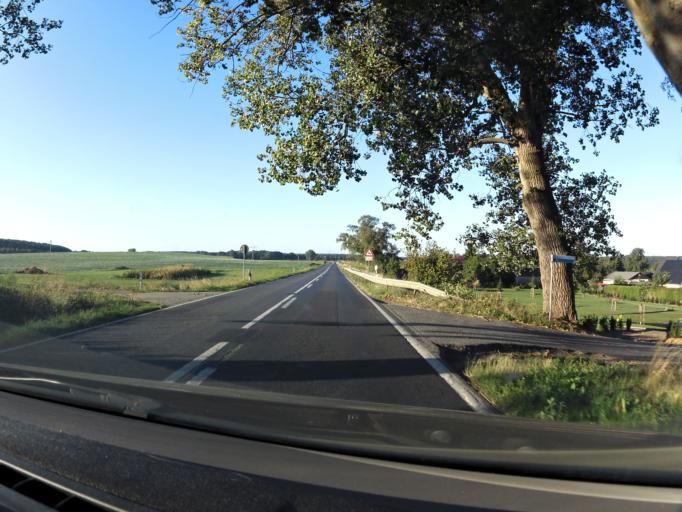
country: DE
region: Mecklenburg-Vorpommern
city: Loddin
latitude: 53.9357
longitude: 14.0373
